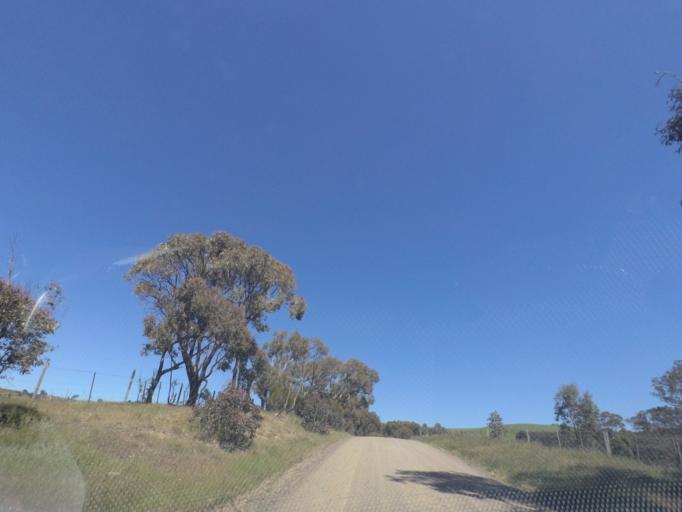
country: AU
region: Victoria
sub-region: Whittlesea
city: Whittlesea
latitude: -37.2763
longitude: 145.0178
